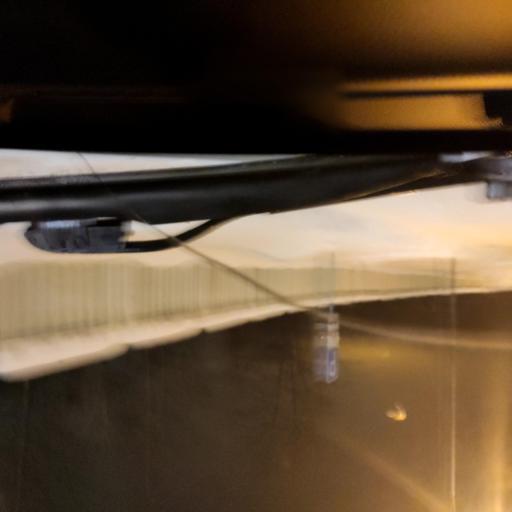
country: RU
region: Tatarstan
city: Staroye Arakchino
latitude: 55.8315
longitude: 49.0339
